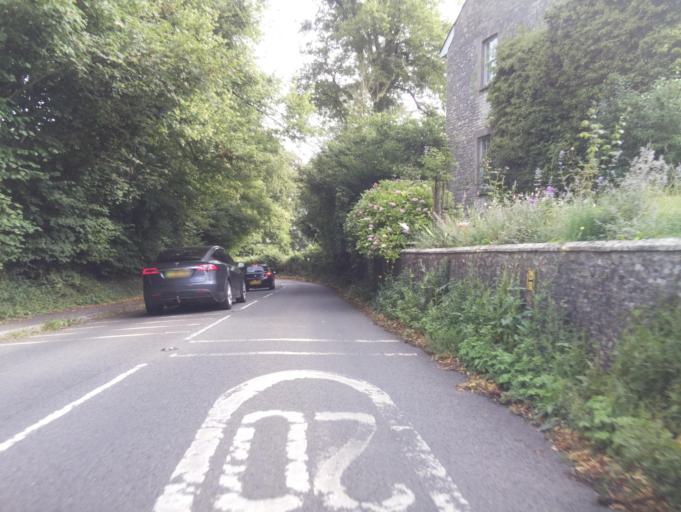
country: GB
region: England
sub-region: Bath and North East Somerset
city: Chew Magna
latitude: 51.3501
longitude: -2.6339
